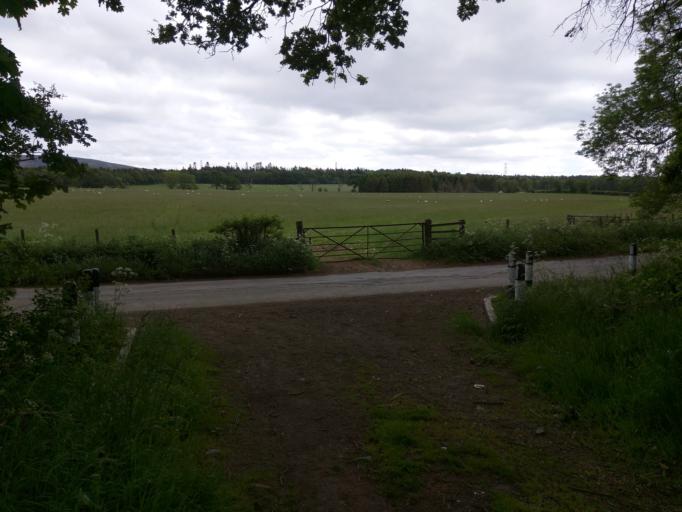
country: GB
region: Scotland
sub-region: Edinburgh
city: Balerno
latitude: 55.8775
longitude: -3.3539
